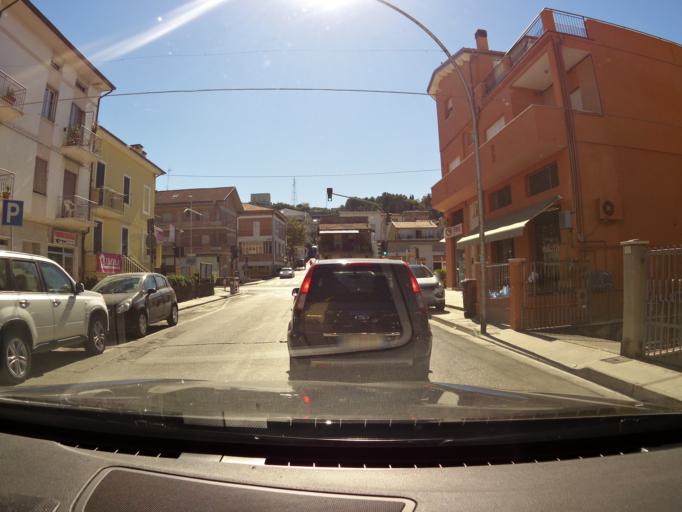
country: IT
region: The Marches
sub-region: Province of Fermo
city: Porto San Giorgio
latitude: 43.1873
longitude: 13.7912
